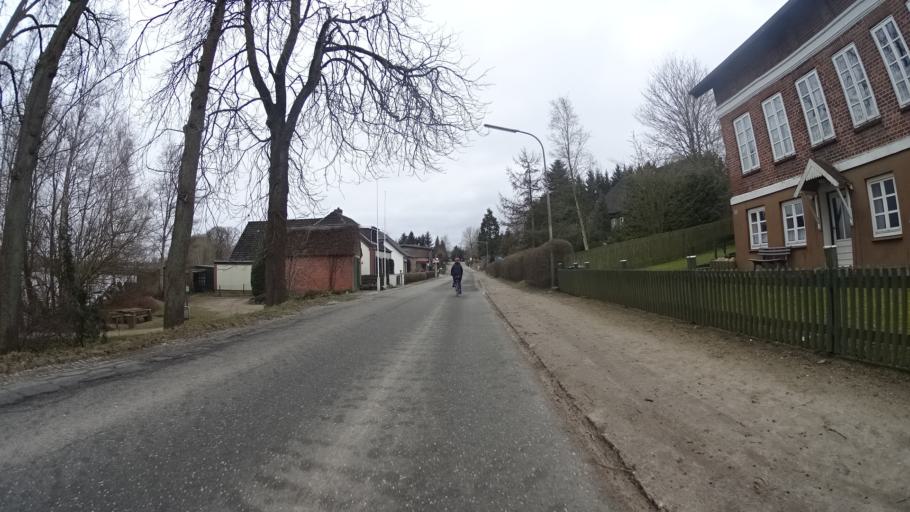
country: DE
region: Schleswig-Holstein
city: Neukirchen
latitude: 54.2165
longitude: 10.5556
